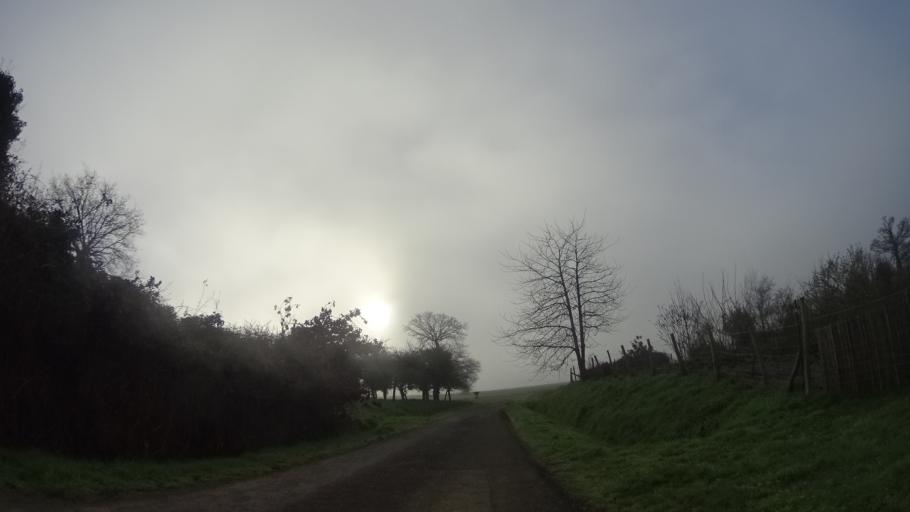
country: FR
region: Brittany
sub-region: Departement des Cotes-d'Armor
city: Evran
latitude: 48.3373
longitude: -1.9609
